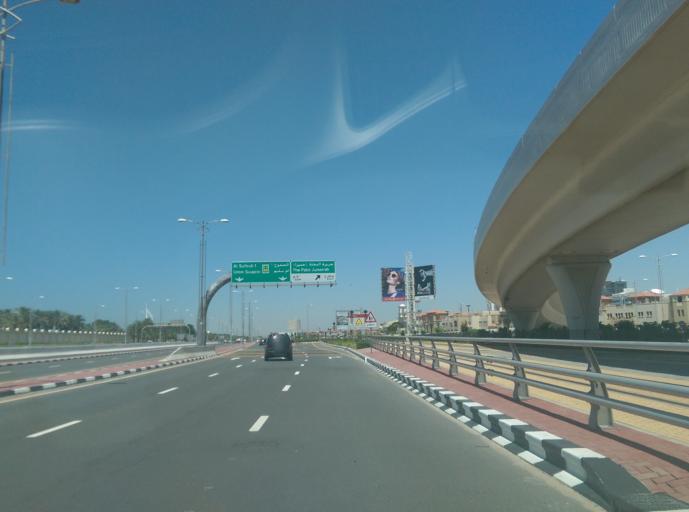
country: AE
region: Dubai
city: Dubai
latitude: 25.1006
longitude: 55.1578
